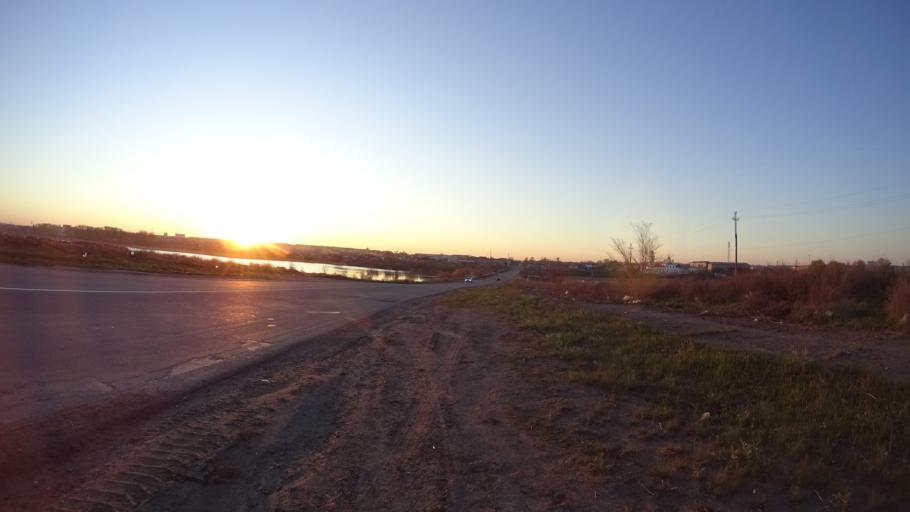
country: RU
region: Chelyabinsk
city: Troitsk
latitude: 54.0725
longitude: 61.5589
